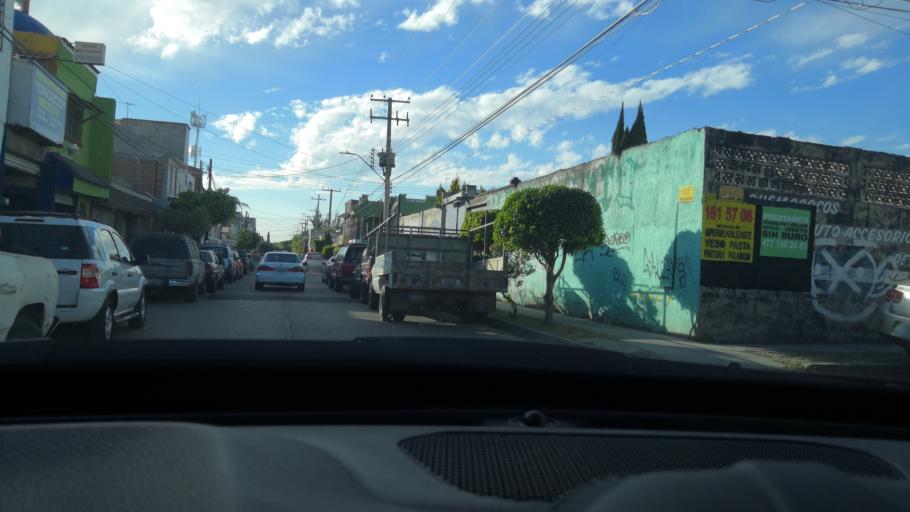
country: MX
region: Guanajuato
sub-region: Leon
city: San Jose de Duran (Los Troncoso)
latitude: 21.0918
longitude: -101.6525
